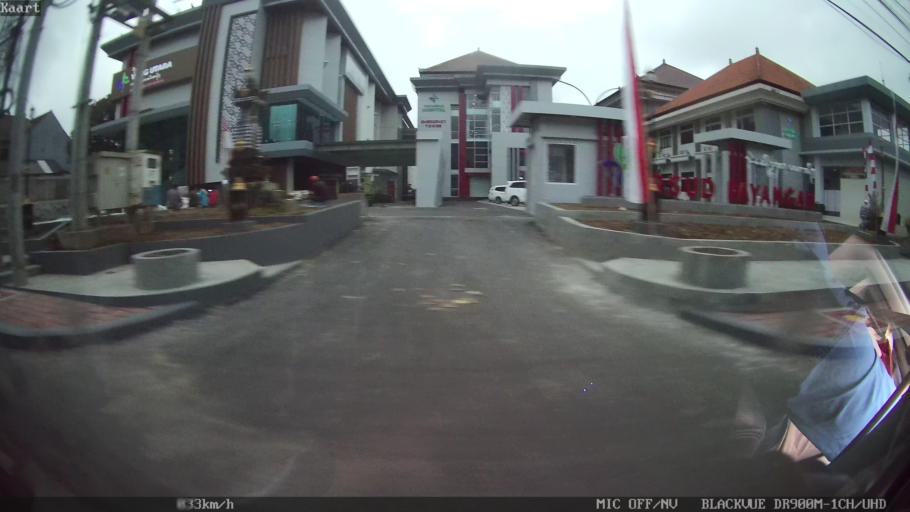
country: ID
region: Bali
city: Badung
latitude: -8.4218
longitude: 115.2452
